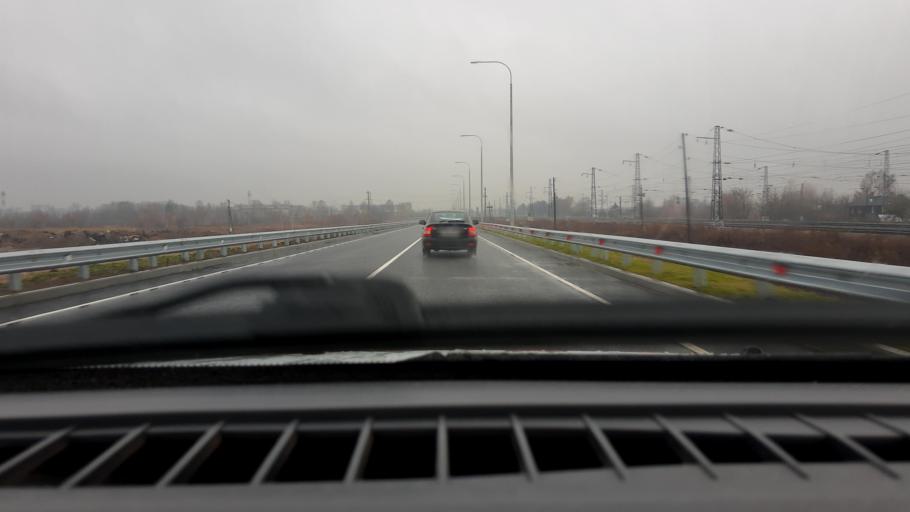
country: RU
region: Nizjnij Novgorod
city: Neklyudovo
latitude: 56.4139
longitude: 43.9834
